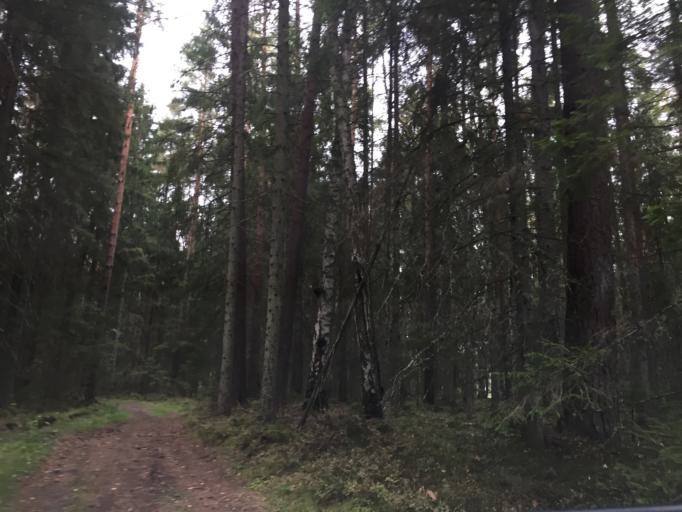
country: LV
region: Baldone
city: Baldone
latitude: 56.7818
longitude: 24.4442
